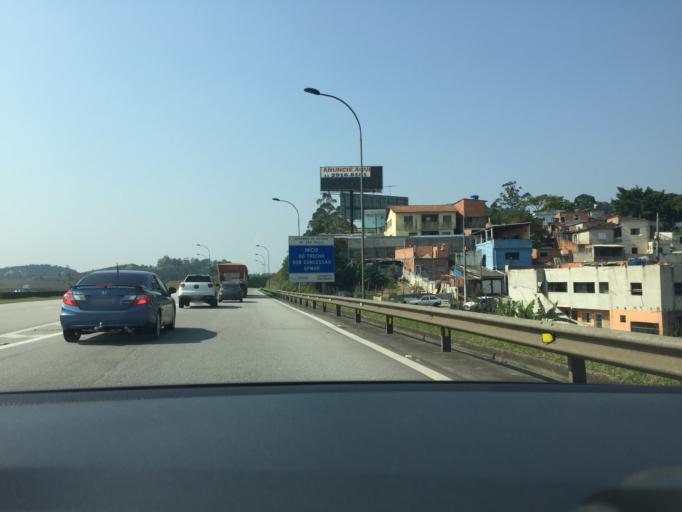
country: BR
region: Sao Paulo
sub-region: Sao Bernardo Do Campo
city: Sao Bernardo do Campo
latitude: -23.7710
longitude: -46.5924
